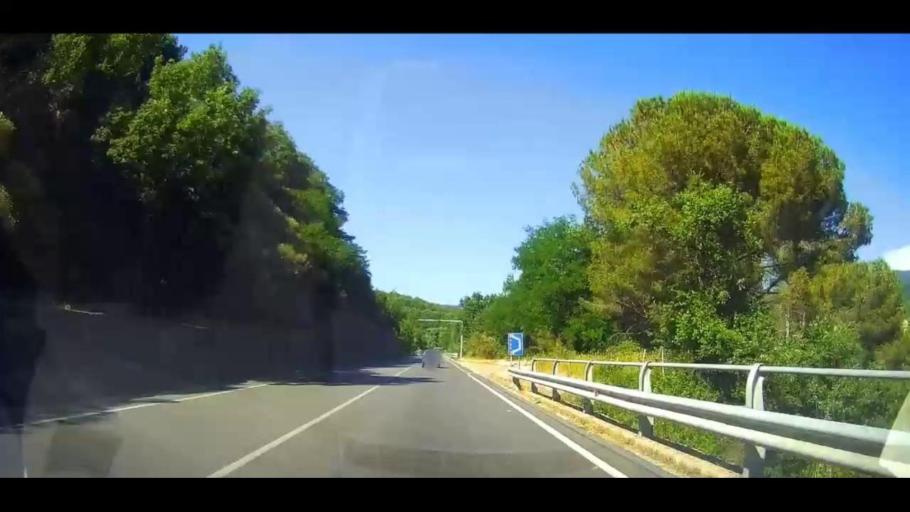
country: IT
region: Calabria
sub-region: Provincia di Cosenza
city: Rovito
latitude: 39.3076
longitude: 16.3246
